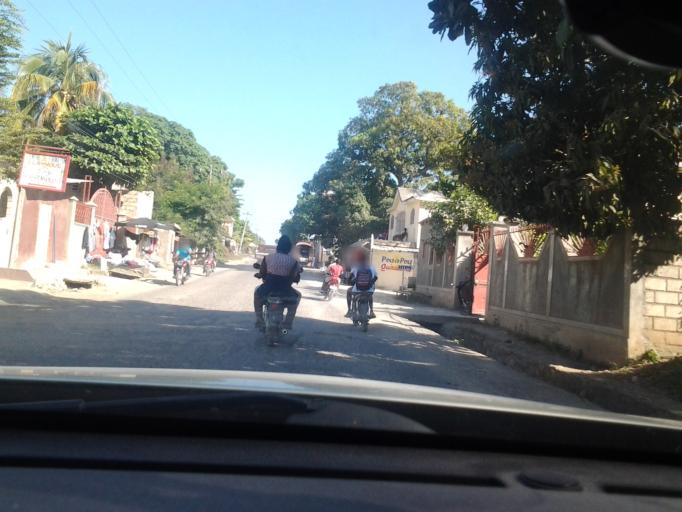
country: HT
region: Sud-Est
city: Jacmel
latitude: 18.2339
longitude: -72.5036
